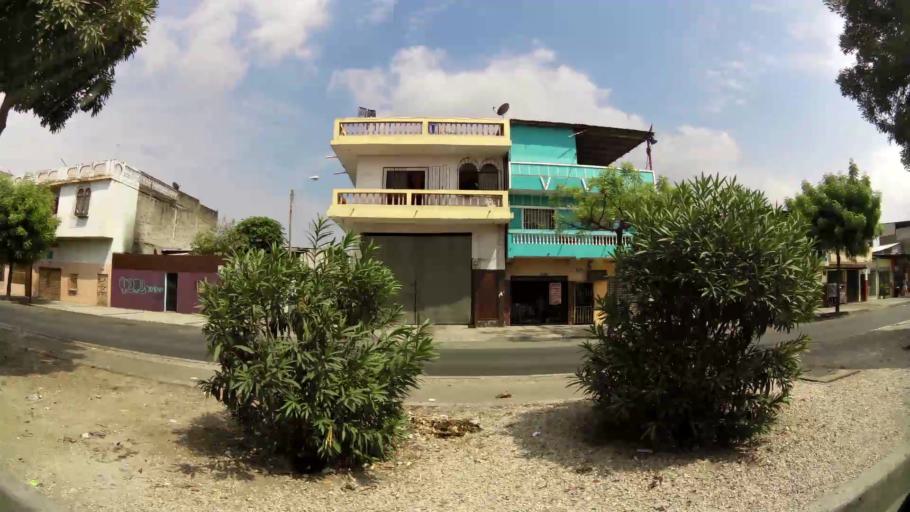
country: EC
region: Guayas
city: Guayaquil
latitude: -2.2674
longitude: -79.8776
